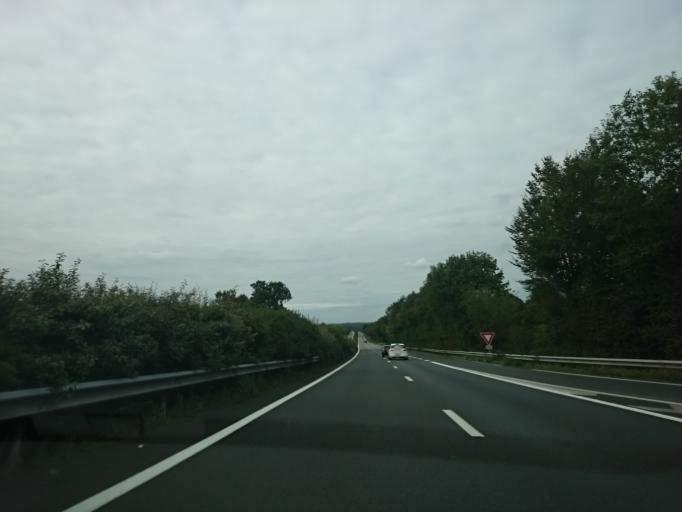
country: FR
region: Pays de la Loire
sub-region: Departement de la Loire-Atlantique
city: Nozay
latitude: 47.5866
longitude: -1.6271
